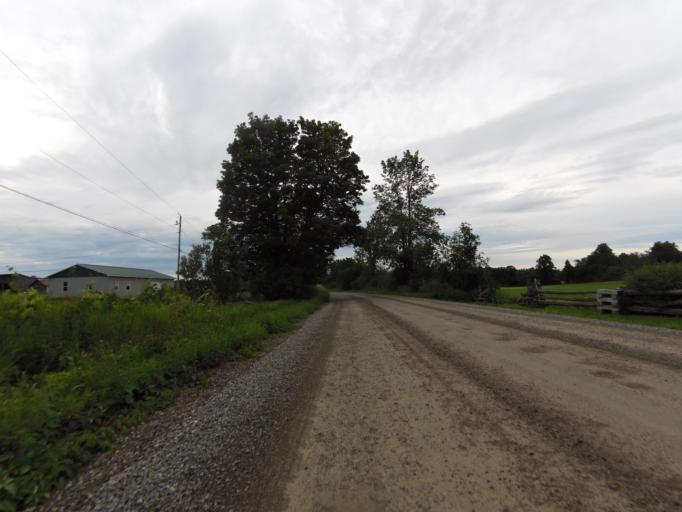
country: CA
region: Ontario
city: Carleton Place
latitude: 45.1506
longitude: -76.1775
